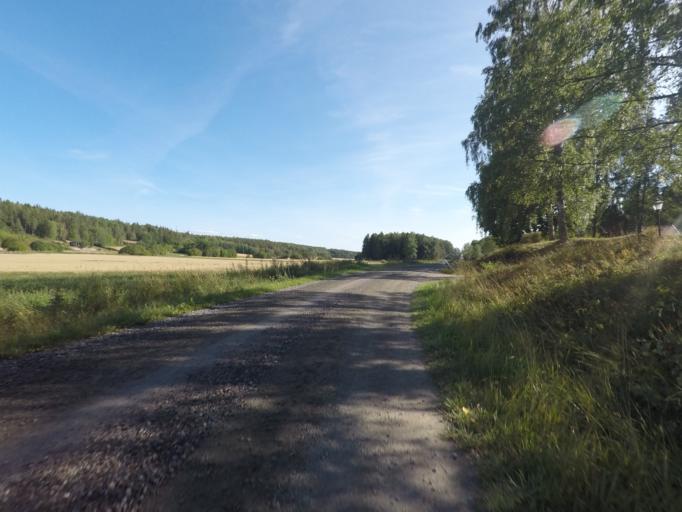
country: SE
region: Soedermanland
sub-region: Eskilstuna Kommun
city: Kvicksund
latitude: 59.4221
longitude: 16.2625
